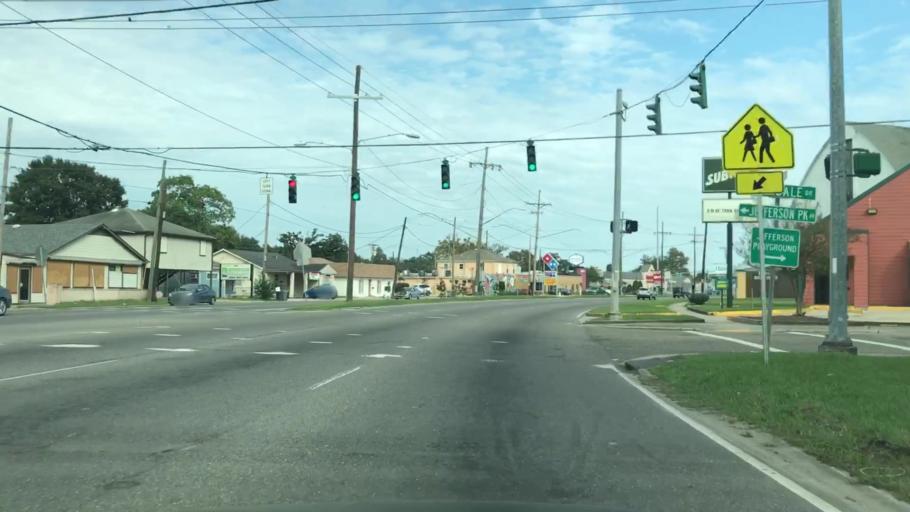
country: US
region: Louisiana
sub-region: Jefferson Parish
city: Jefferson
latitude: 29.9629
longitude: -90.1661
